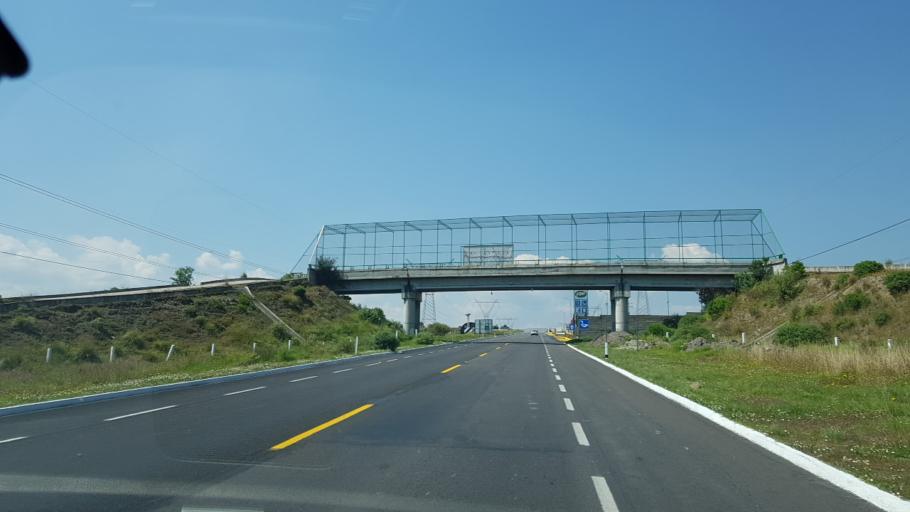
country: MX
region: Mexico
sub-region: Almoloya de Juarez
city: San Pedro de la Hortaliza (Ejido Almoloyan)
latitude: 19.3802
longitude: -99.8181
